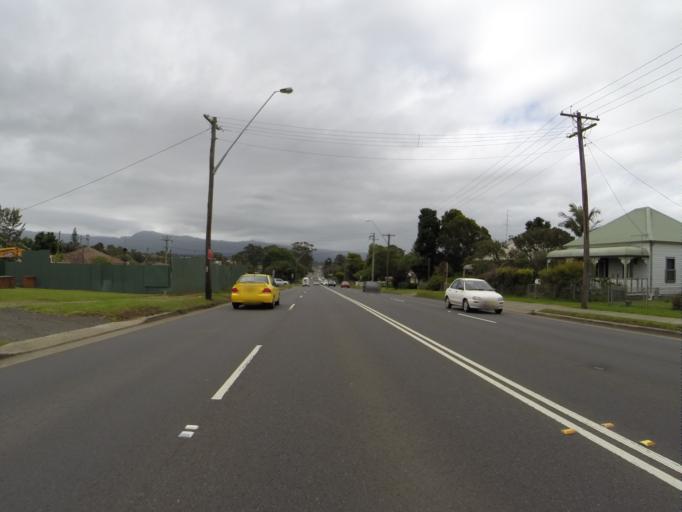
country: AU
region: New South Wales
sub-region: Shoalhaven Shire
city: Nowra
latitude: -34.8838
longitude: 150.6037
